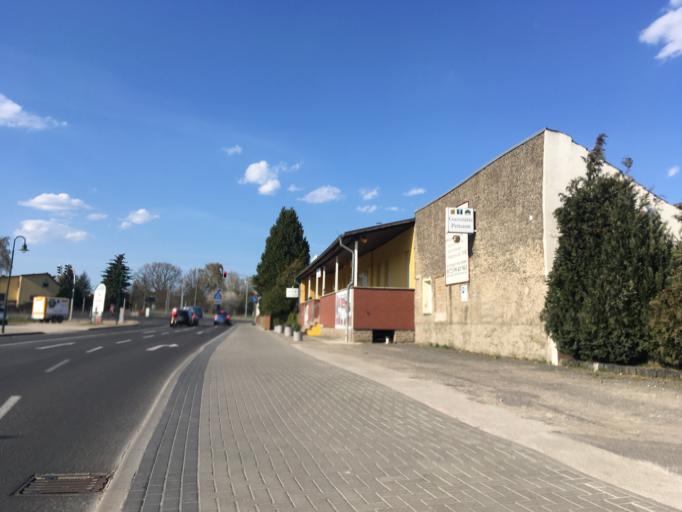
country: DE
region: Berlin
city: Wartenberg
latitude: 52.6035
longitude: 13.5240
